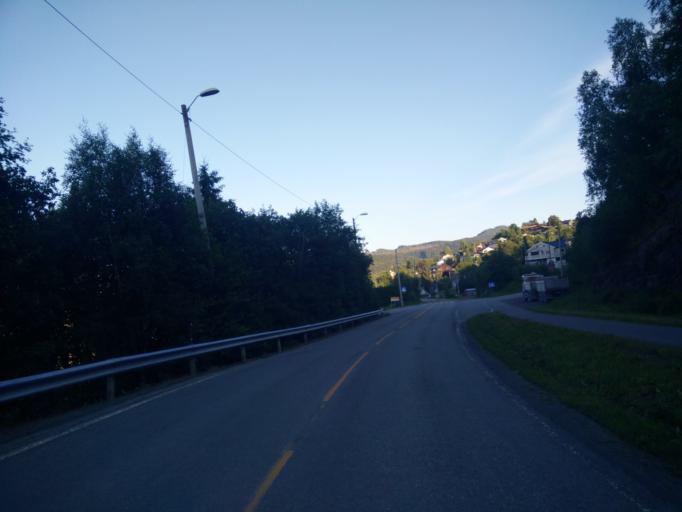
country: NO
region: Sor-Trondelag
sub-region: Skaun
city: Borsa
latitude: 63.3383
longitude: 10.0590
